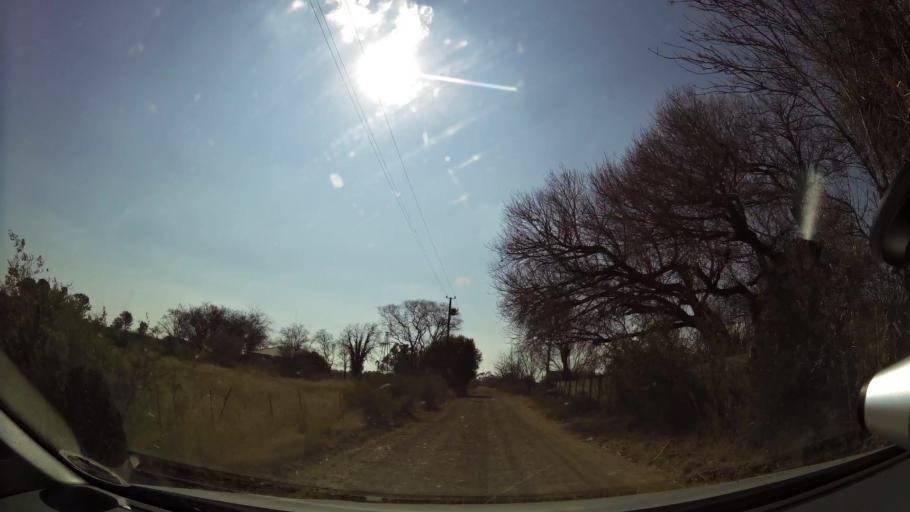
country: ZA
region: Orange Free State
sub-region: Mangaung Metropolitan Municipality
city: Bloemfontein
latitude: -29.1637
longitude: 26.3109
